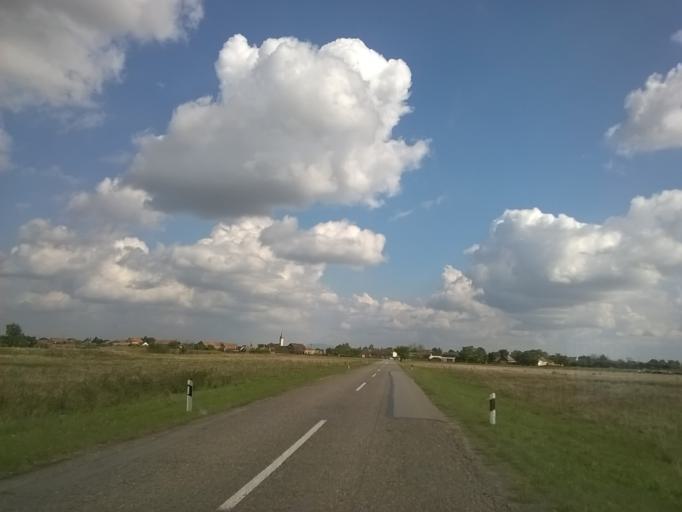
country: RS
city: Barice
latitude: 45.1820
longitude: 21.0700
